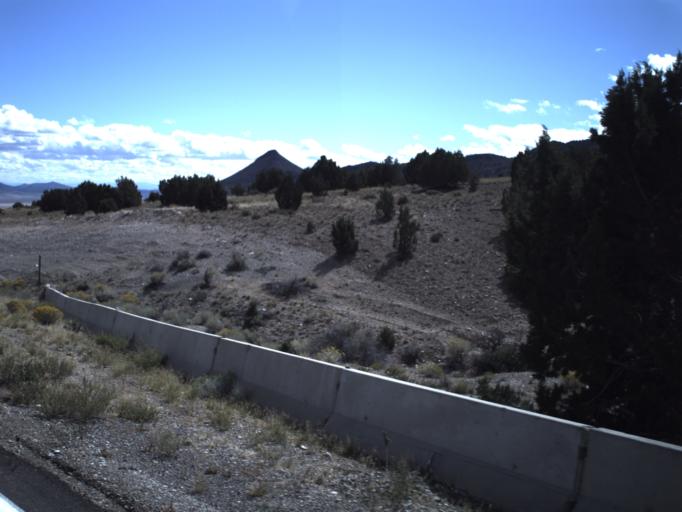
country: US
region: Utah
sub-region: Beaver County
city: Milford
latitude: 38.5083
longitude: -113.5185
